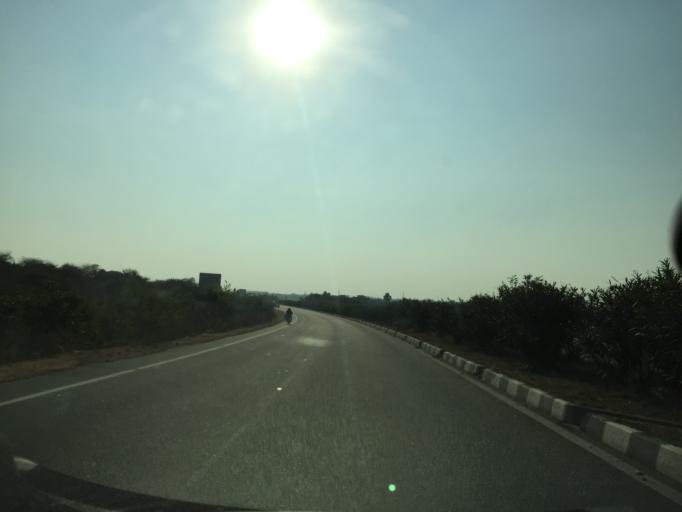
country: IN
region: Telangana
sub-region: Nalgonda
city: Bhongir
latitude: 17.5125
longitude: 78.9022
